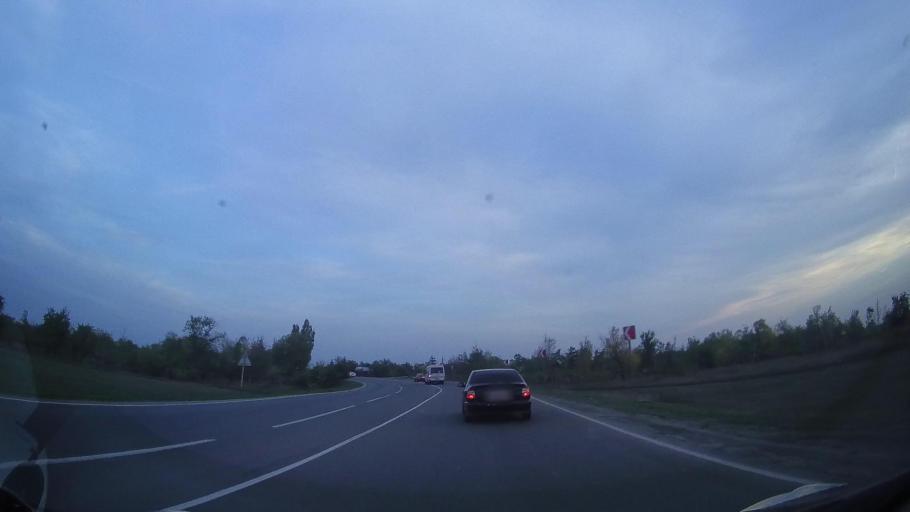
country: RU
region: Rostov
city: Kagal'nitskaya
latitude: 46.8919
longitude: 40.1306
